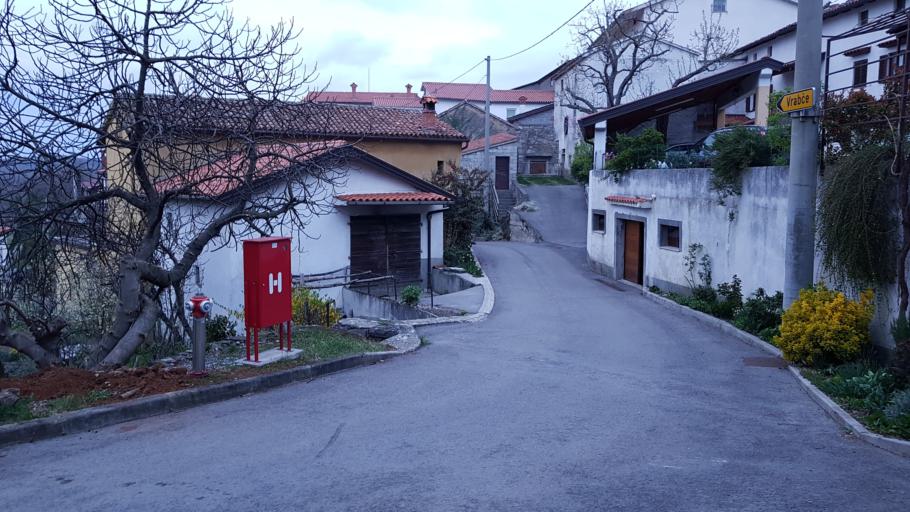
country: SI
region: Vipava
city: Vipava
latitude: 45.7669
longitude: 13.9779
